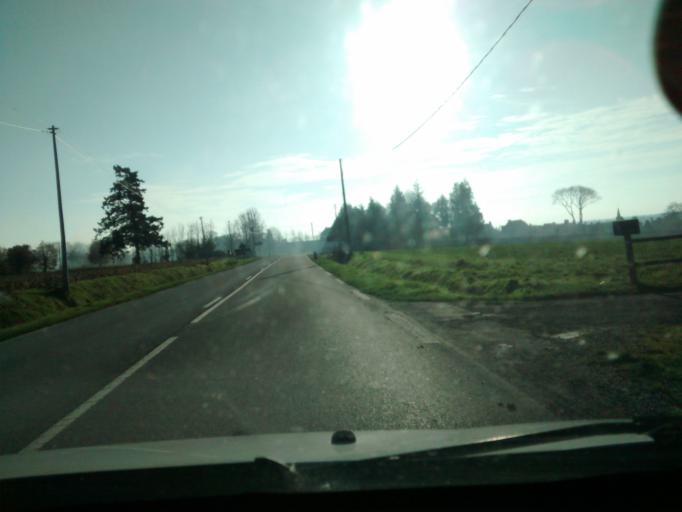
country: FR
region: Brittany
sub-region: Departement d'Ille-et-Vilaine
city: Tremblay
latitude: 48.3791
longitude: -1.4938
